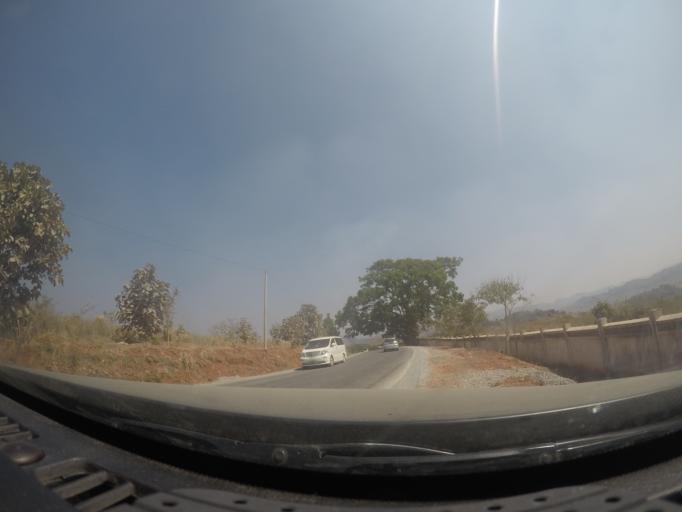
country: MM
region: Shan
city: Taunggyi
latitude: 20.8065
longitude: 97.1989
